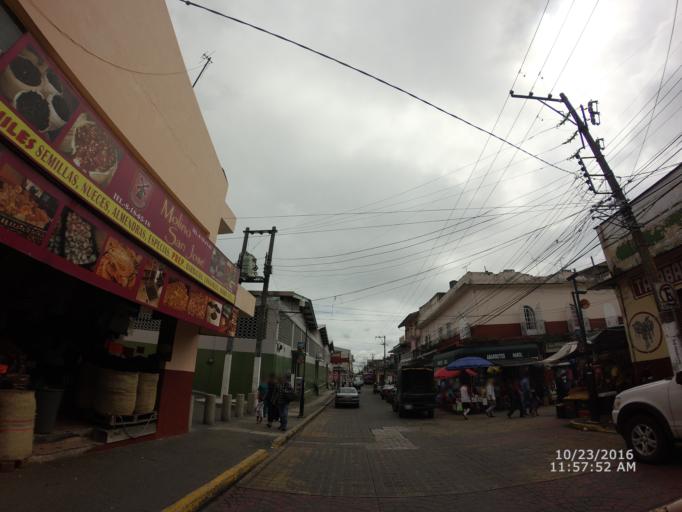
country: MX
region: Veracruz
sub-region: Xalapa
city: Xalapa de Enriquez
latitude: 19.5329
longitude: -96.9222
